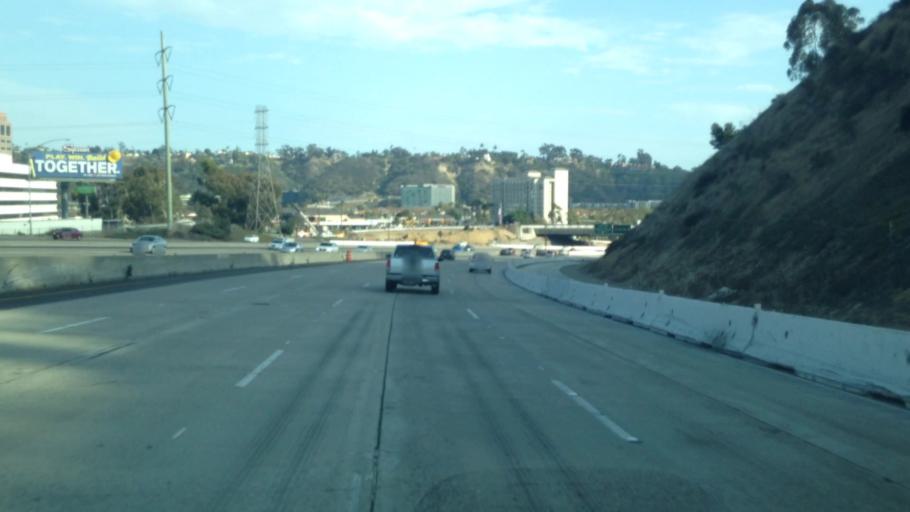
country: US
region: California
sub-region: San Diego County
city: San Diego
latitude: 32.7753
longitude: -117.1617
